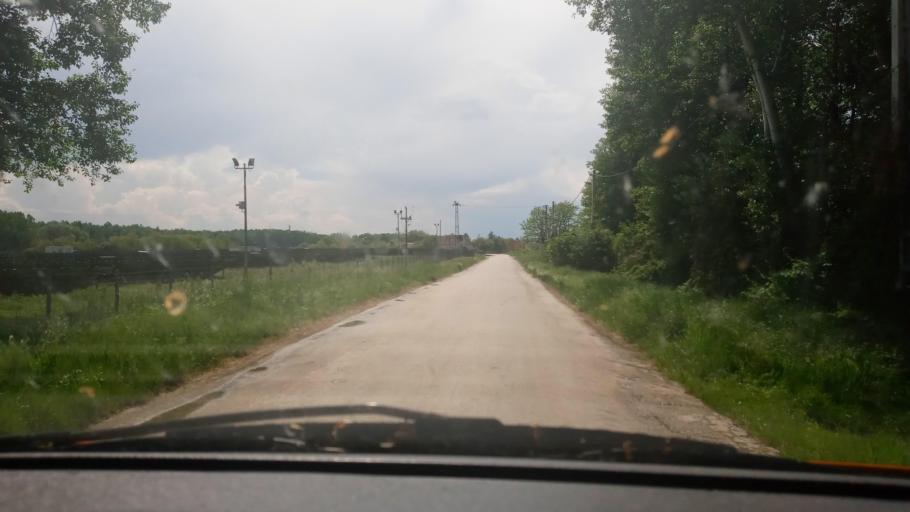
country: HU
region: Baranya
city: Siklos
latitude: 45.8135
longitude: 18.3420
